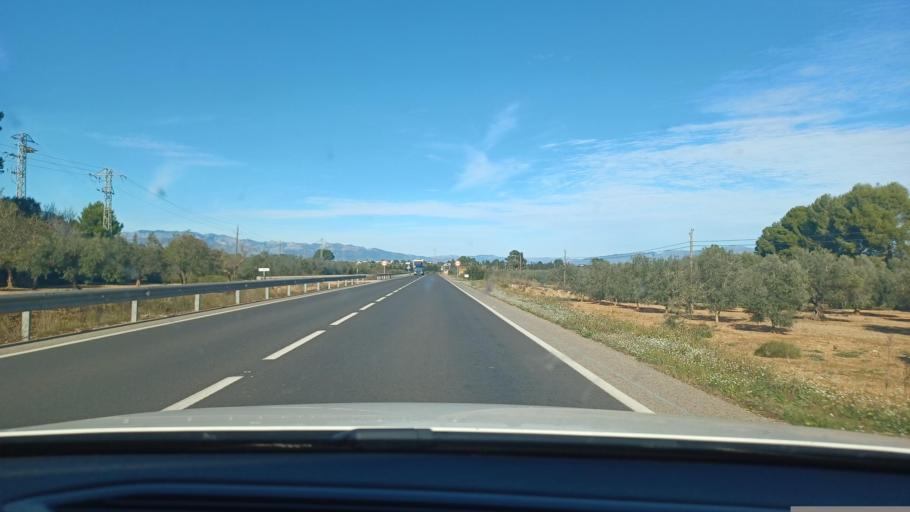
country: ES
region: Catalonia
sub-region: Provincia de Tarragona
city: Santa Barbara
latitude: 40.6931
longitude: 0.5061
